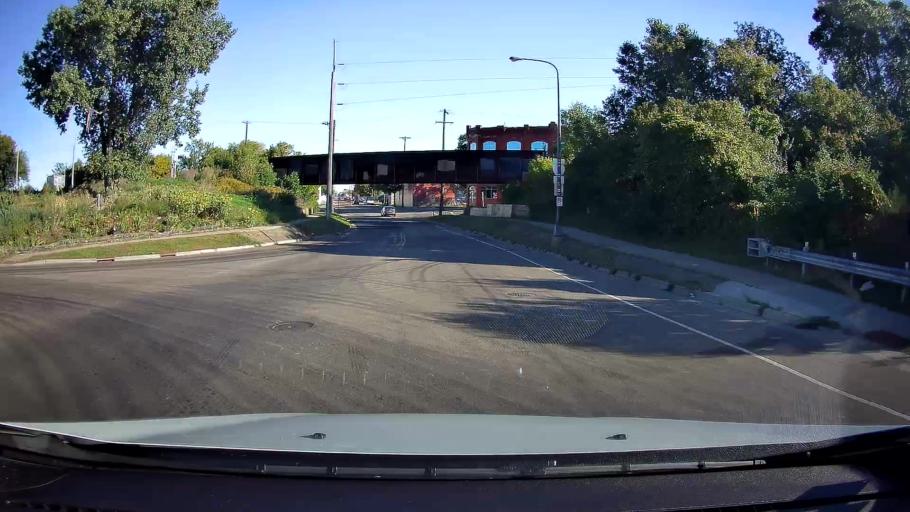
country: US
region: Minnesota
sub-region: Ramsey County
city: Falcon Heights
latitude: 44.9532
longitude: -93.1824
